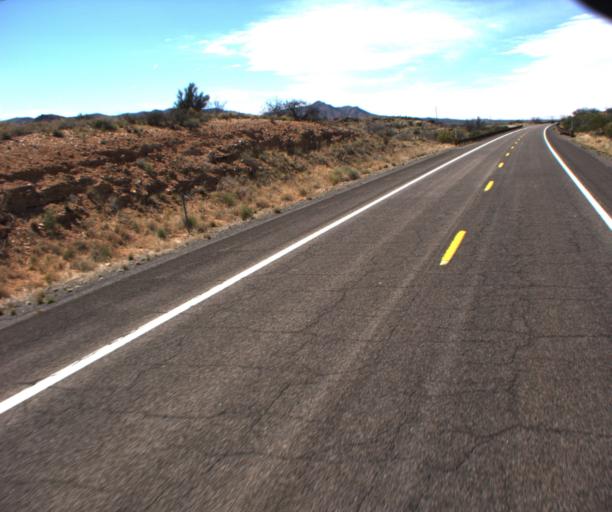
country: US
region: Arizona
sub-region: Mohave County
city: Peach Springs
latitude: 35.3668
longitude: -113.7111
